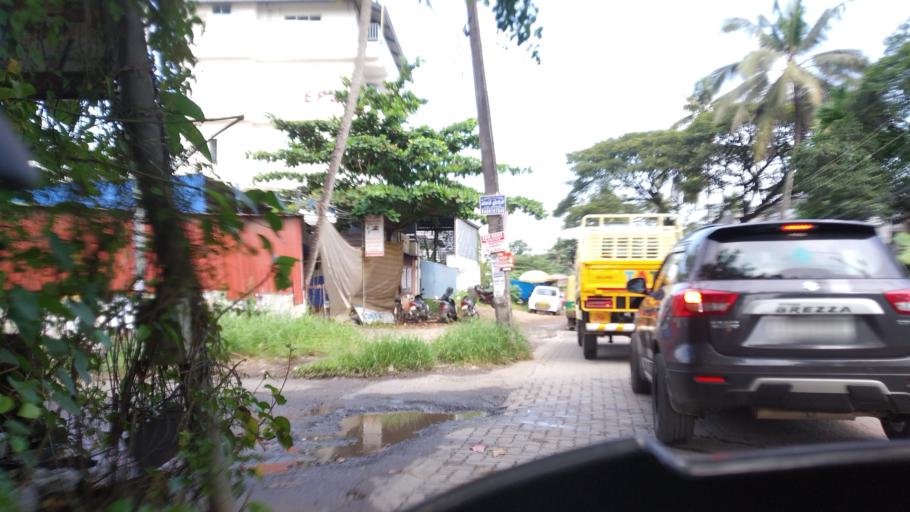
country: IN
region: Kerala
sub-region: Ernakulam
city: Cochin
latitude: 9.9833
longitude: 76.2993
